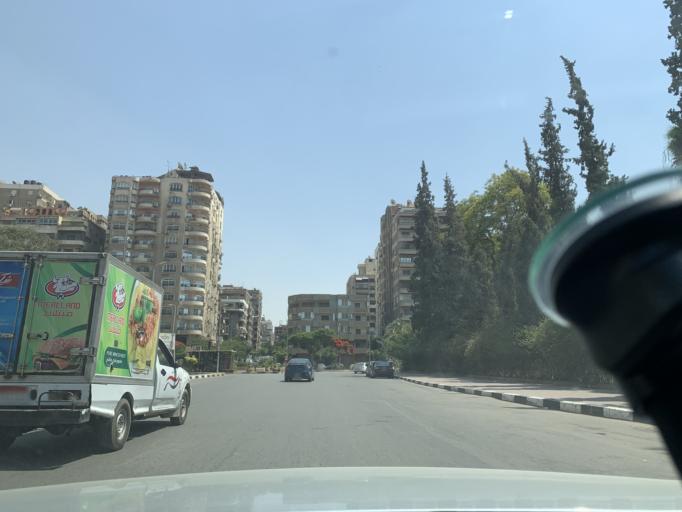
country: EG
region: Muhafazat al Qahirah
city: Cairo
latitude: 30.0617
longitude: 31.3496
